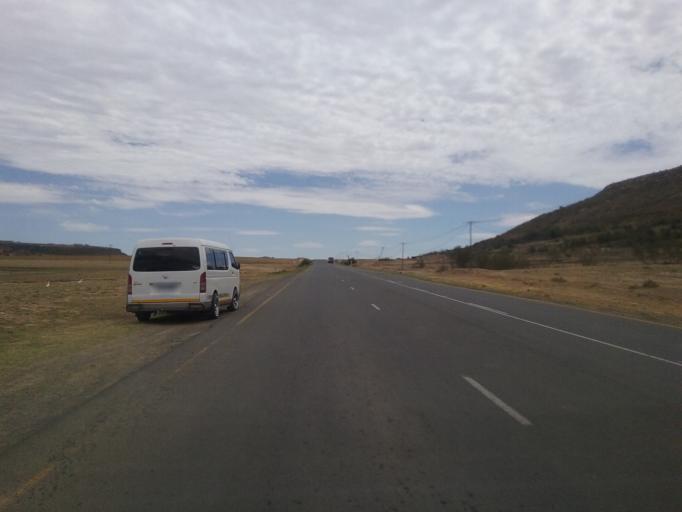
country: LS
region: Maseru
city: Nako
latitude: -29.6067
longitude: 27.5012
